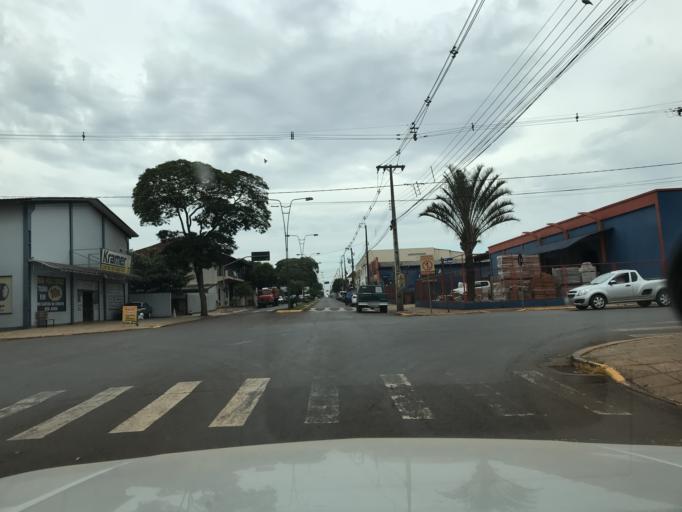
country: BR
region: Parana
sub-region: Marechal Candido Rondon
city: Marechal Candido Rondon
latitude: -24.4631
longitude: -53.9517
